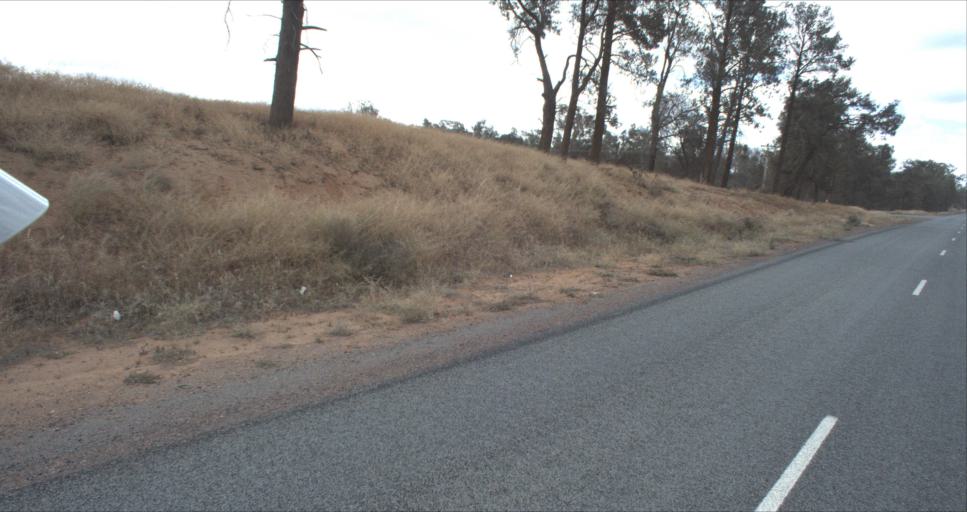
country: AU
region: New South Wales
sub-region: Leeton
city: Leeton
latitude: -34.6592
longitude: 146.3497
